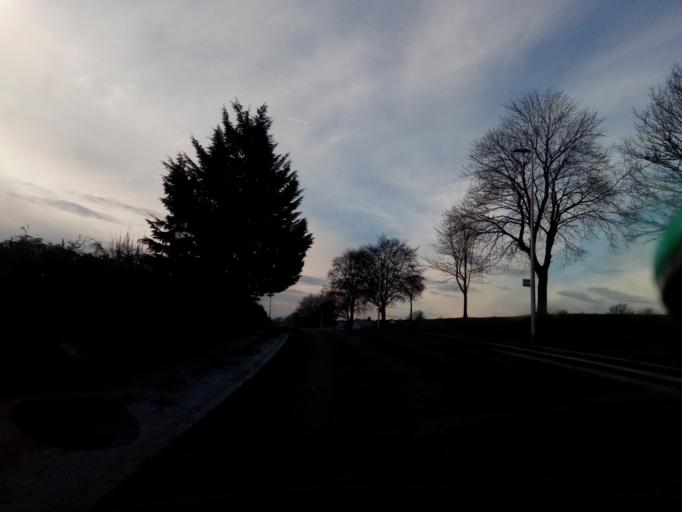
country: GB
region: Scotland
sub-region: The Scottish Borders
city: Hawick
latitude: 55.4382
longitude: -2.7606
